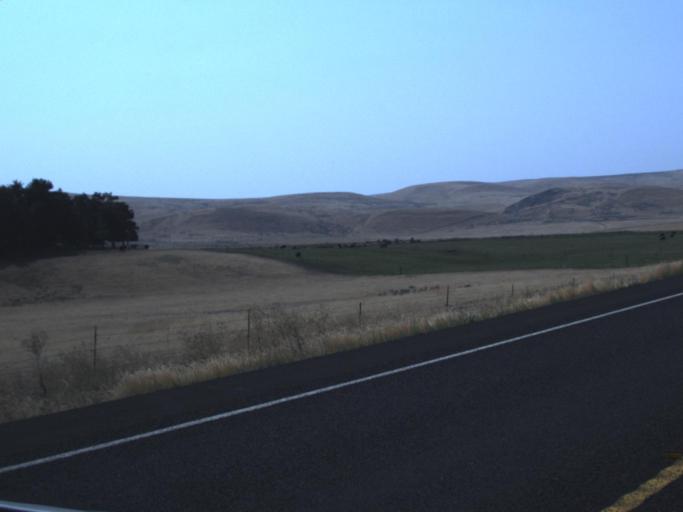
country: US
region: Washington
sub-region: Yakima County
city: Zillah
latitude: 46.5012
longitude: -120.1345
